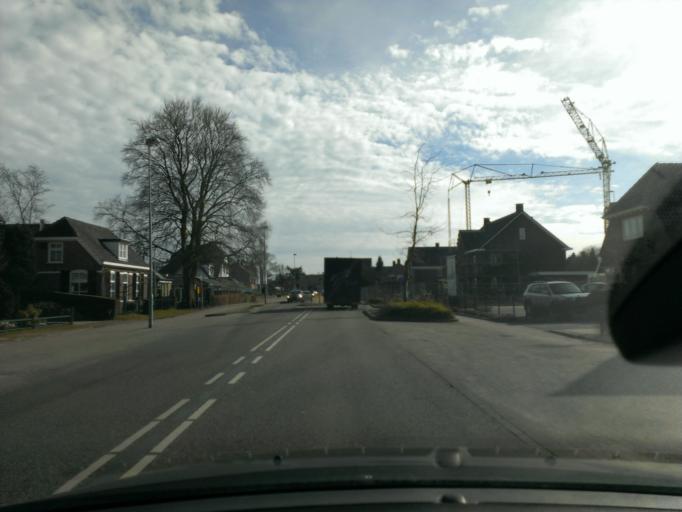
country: NL
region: Gelderland
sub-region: Gemeente Hattem
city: Hattem
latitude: 52.4652
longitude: 5.9908
